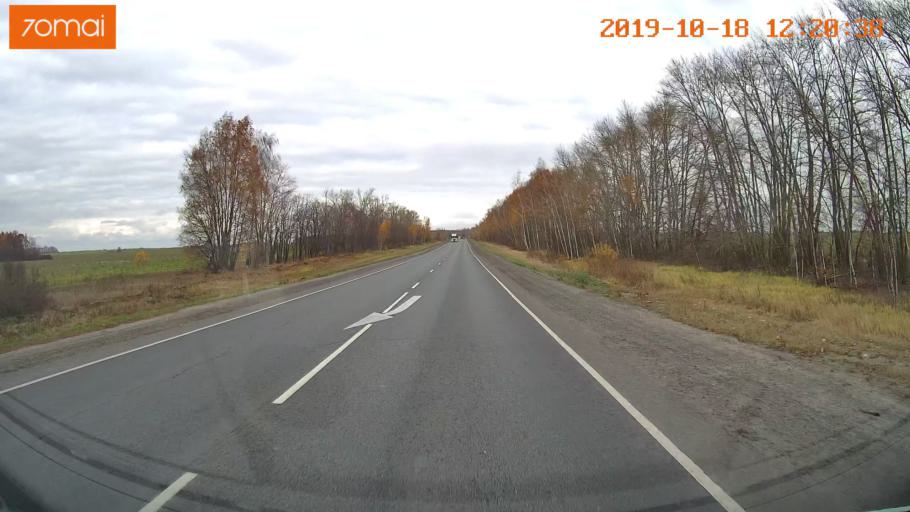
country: RU
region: Rjazan
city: Bagramovo
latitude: 54.5004
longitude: 39.4826
